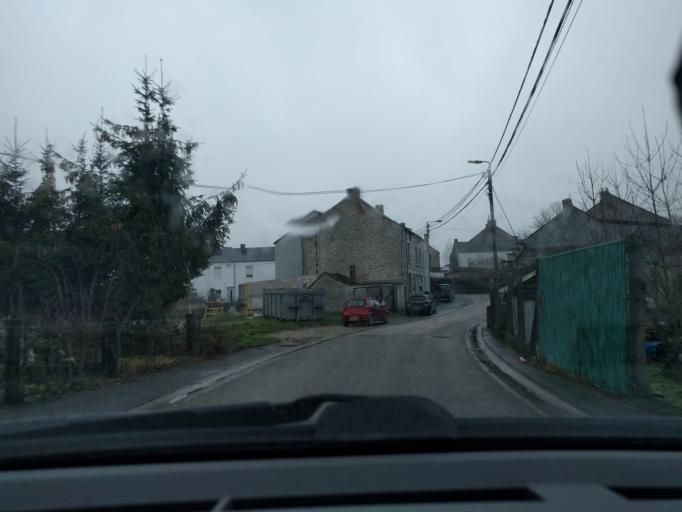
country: BE
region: Wallonia
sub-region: Province de Namur
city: Couvin
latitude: 50.0493
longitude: 4.5027
